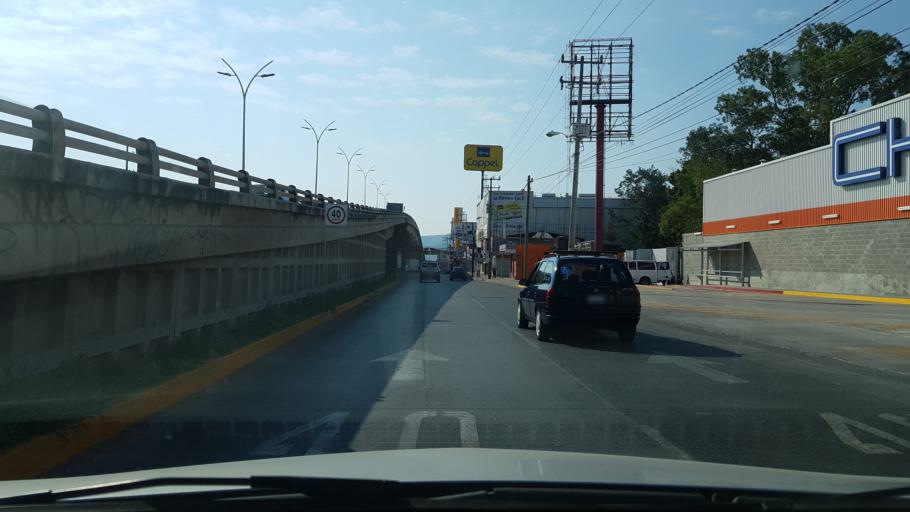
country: MX
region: Morelos
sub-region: Jiutepec
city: Jiutepec
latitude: 18.8986
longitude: -99.1704
